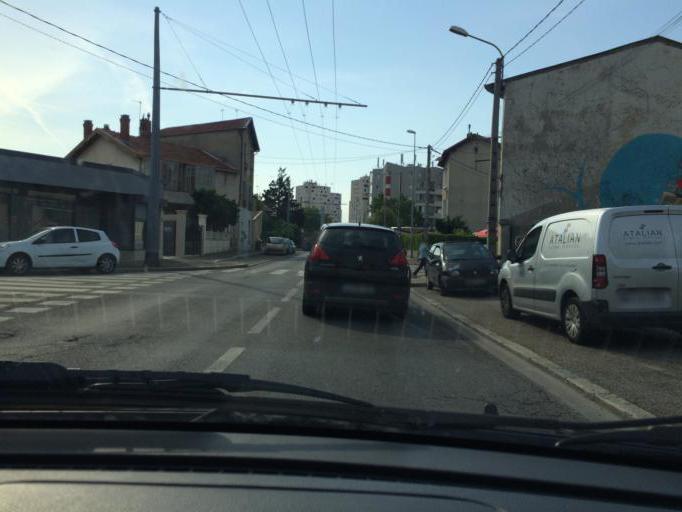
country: FR
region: Rhone-Alpes
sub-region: Departement du Rhone
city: Vaulx-en-Velin
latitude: 45.7624
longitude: 4.9161
